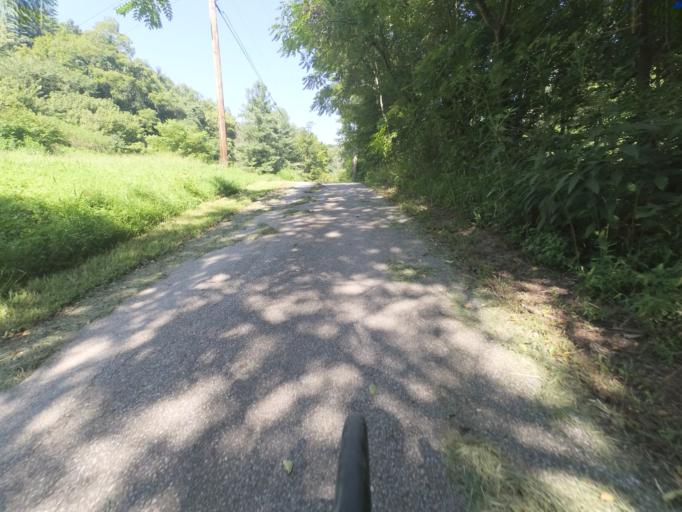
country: US
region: West Virginia
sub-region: Cabell County
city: Huntington
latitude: 38.3874
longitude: -82.4742
